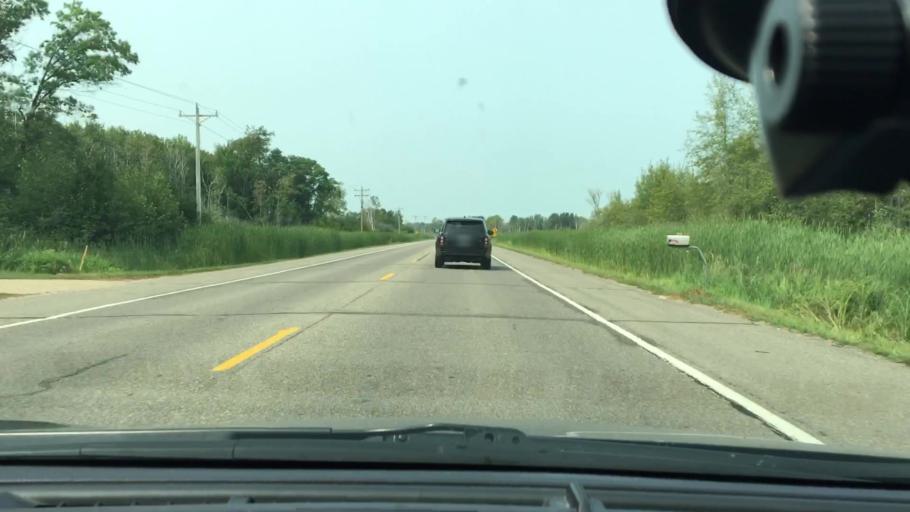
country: US
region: Minnesota
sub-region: Crow Wing County
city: Brainerd
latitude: 46.3985
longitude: -94.2151
